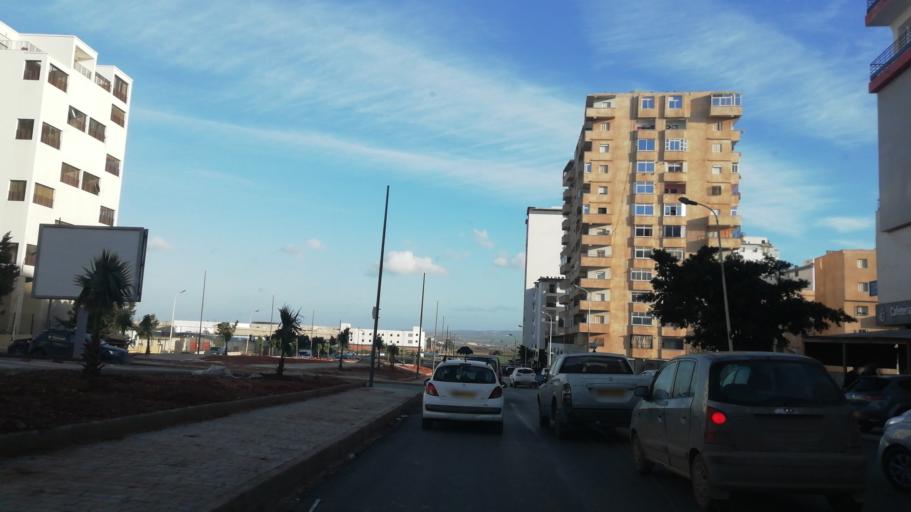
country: DZ
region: Oran
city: Bir el Djir
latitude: 35.7054
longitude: -0.5564
